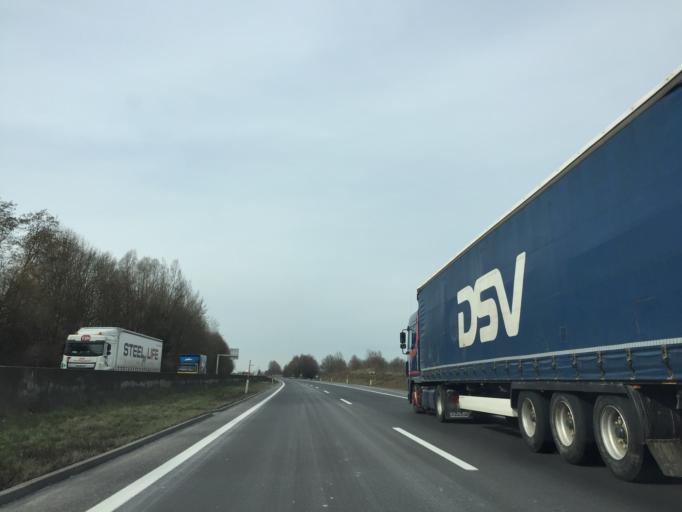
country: AT
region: Upper Austria
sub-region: Politischer Bezirk Scharding
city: Sankt Marienkirchen bei Schaerding
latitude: 48.3059
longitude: 13.4597
